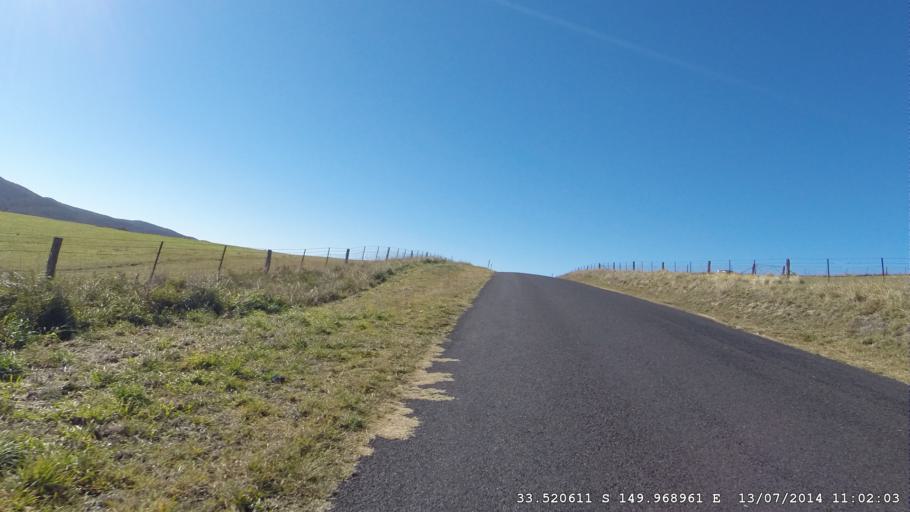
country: AU
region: New South Wales
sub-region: Lithgow
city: Bowenfels
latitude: -33.5206
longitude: 149.9690
